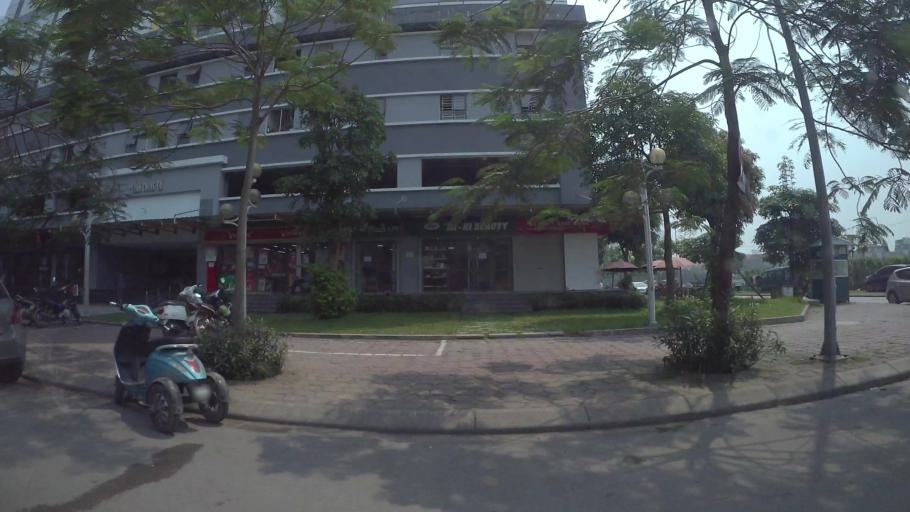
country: VN
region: Ha Noi
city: Van Dien
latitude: 20.9628
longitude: 105.8225
